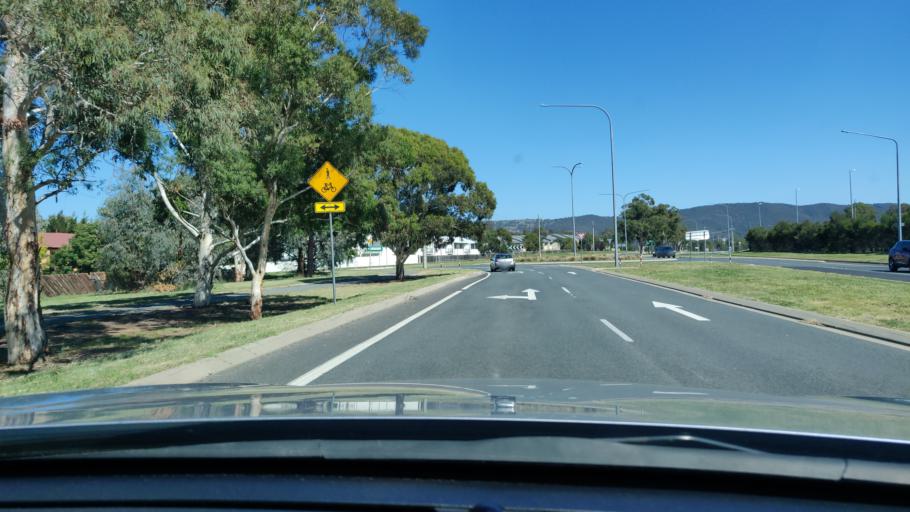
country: AU
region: Australian Capital Territory
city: Macarthur
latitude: -35.4249
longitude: 149.0735
